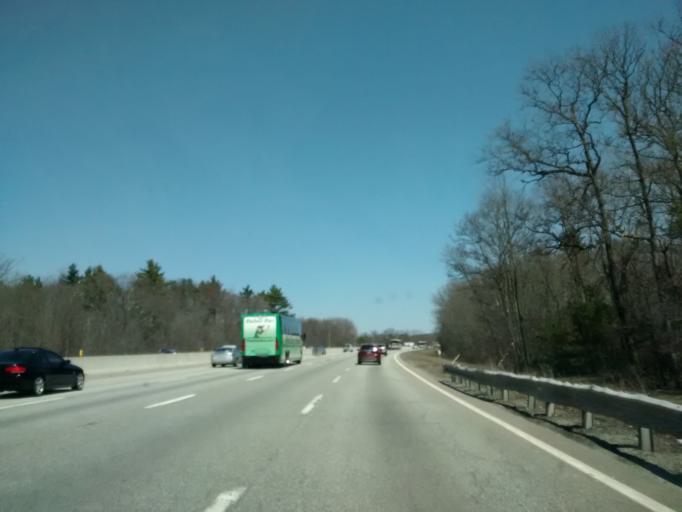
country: US
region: Massachusetts
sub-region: Worcester County
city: Westborough
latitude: 42.2600
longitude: -71.5767
